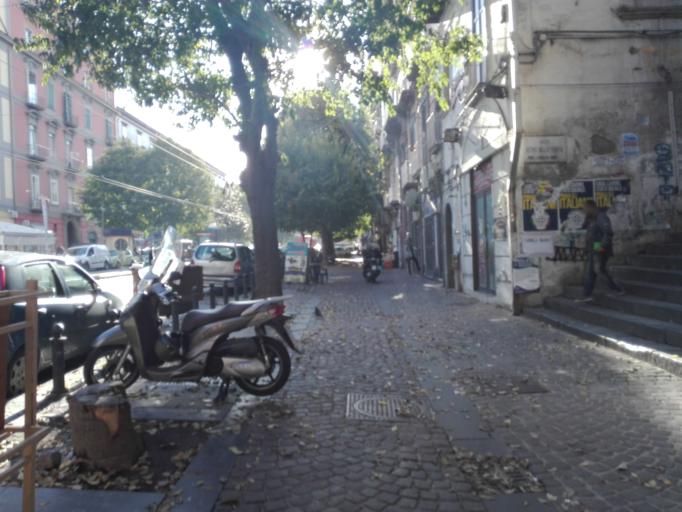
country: IT
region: Campania
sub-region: Provincia di Napoli
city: Napoli
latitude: 40.8587
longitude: 14.2613
